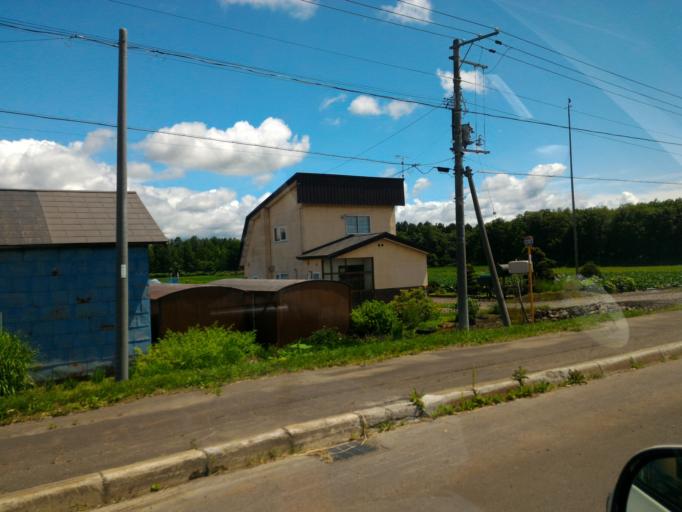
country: JP
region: Hokkaido
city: Nayoro
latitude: 44.5120
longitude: 142.3319
